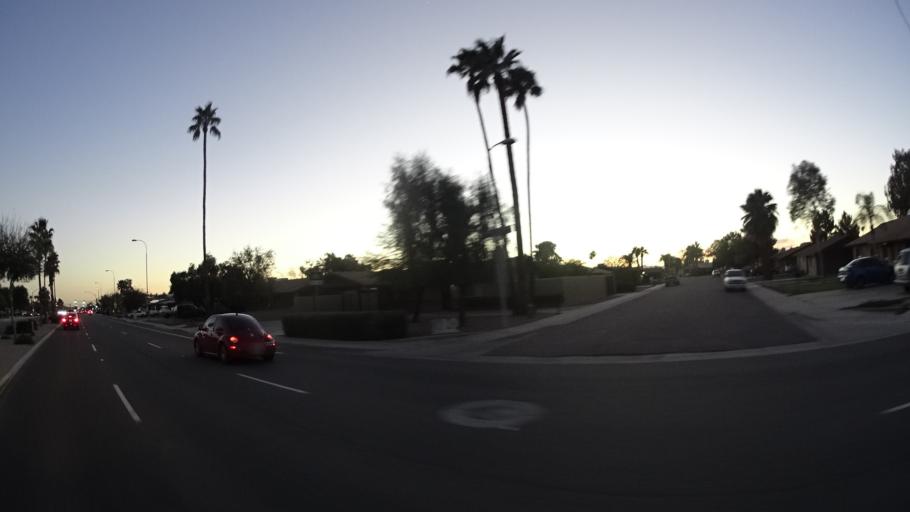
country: US
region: Arizona
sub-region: Maricopa County
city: Chandler
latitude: 33.3005
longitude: -111.8763
